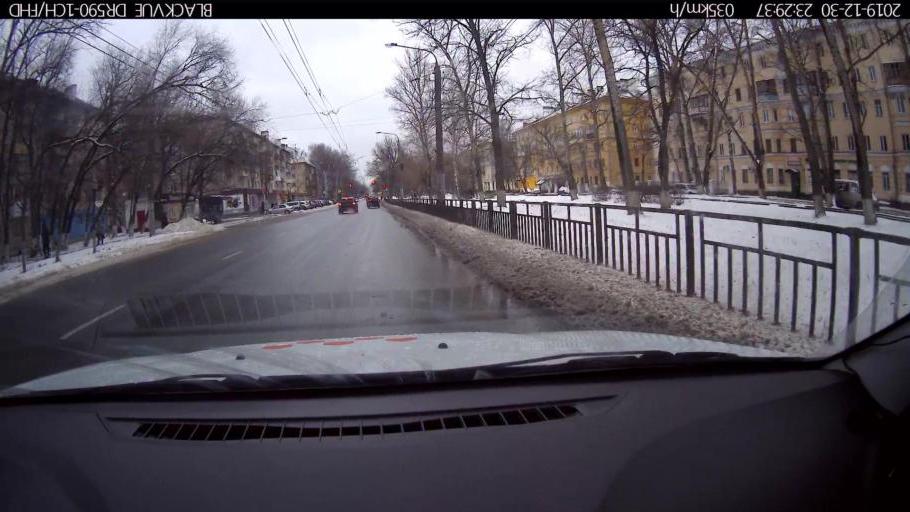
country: RU
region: Nizjnij Novgorod
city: Nizhniy Novgorod
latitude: 56.2829
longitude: 43.9298
